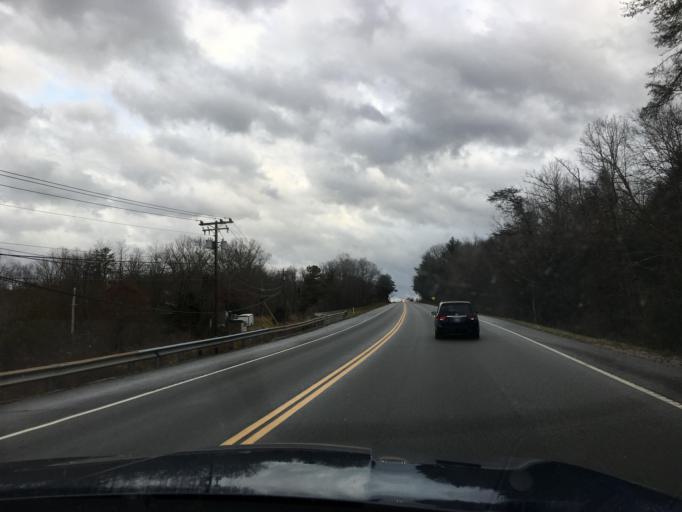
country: US
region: Tennessee
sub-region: Cumberland County
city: Crossville
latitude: 35.9111
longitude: -84.9913
